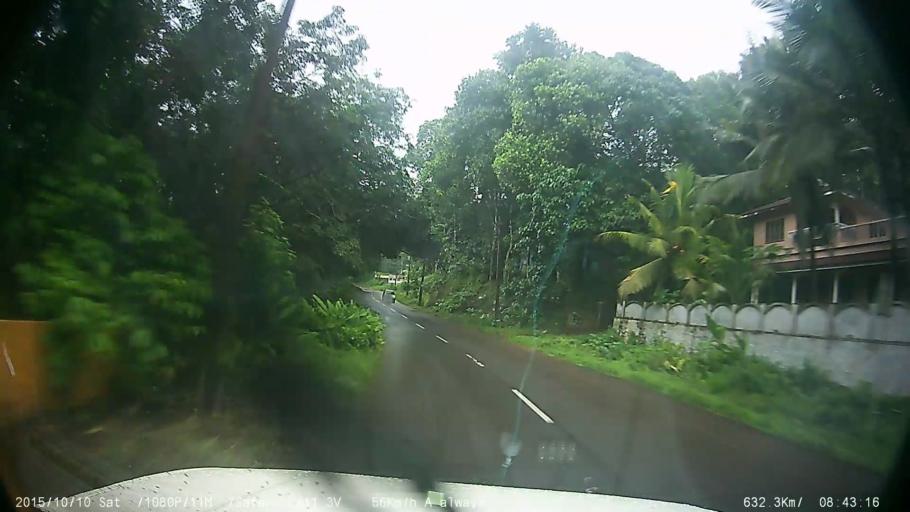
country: IN
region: Kerala
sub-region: Kottayam
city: Palackattumala
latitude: 9.7482
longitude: 76.5359
